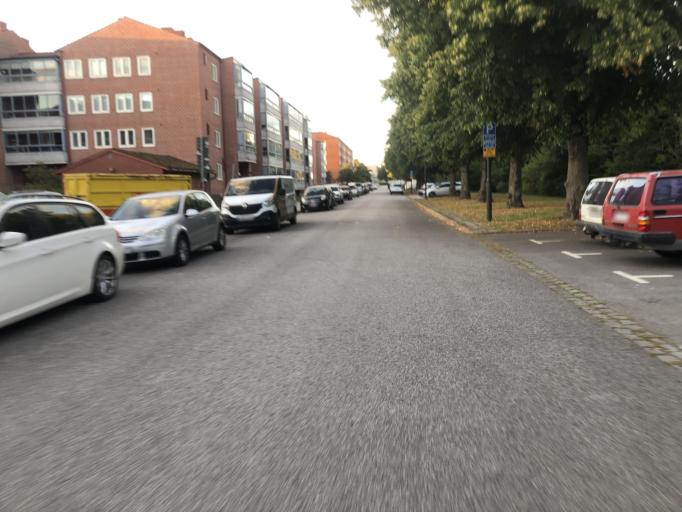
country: SE
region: Skane
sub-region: Malmo
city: Malmoe
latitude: 55.5915
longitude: 13.0315
